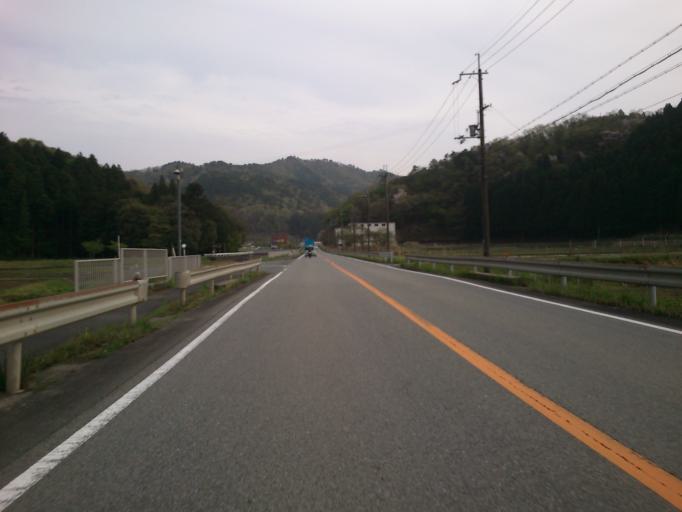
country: JP
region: Hyogo
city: Sasayama
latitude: 35.1235
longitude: 135.3364
